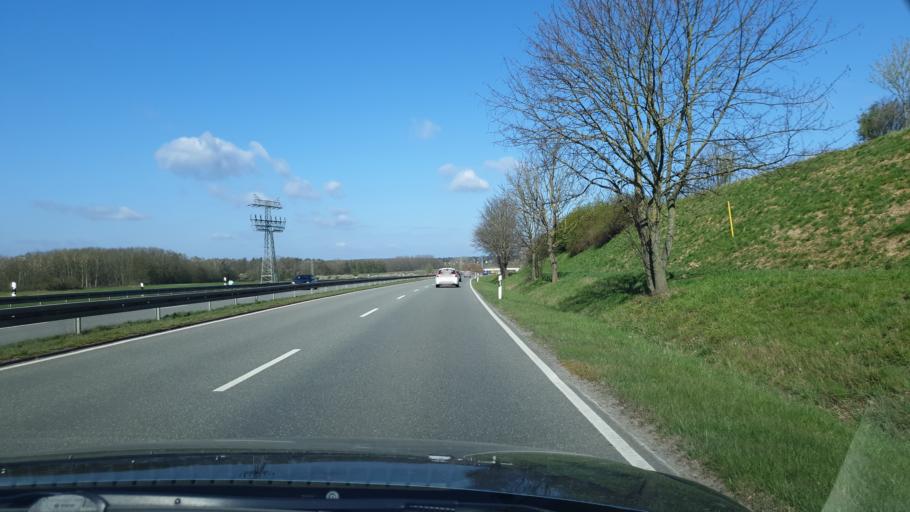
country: DE
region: Mecklenburg-Vorpommern
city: Neumuehle
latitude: 53.6357
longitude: 11.3573
